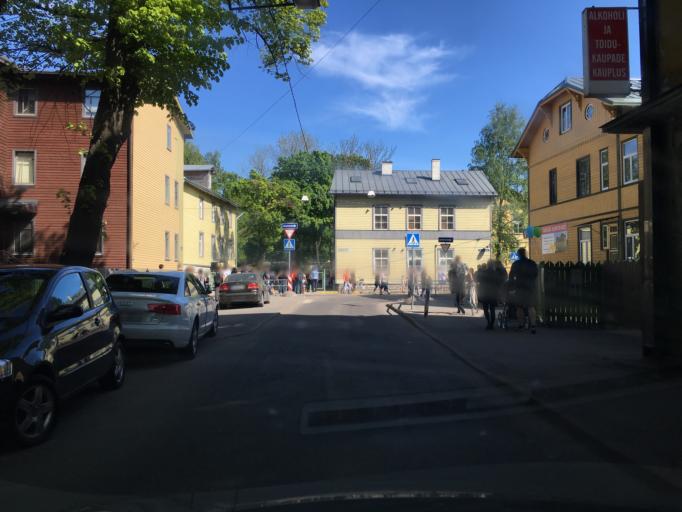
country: EE
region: Harju
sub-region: Tallinna linn
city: Tallinn
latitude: 59.4446
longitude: 24.7375
